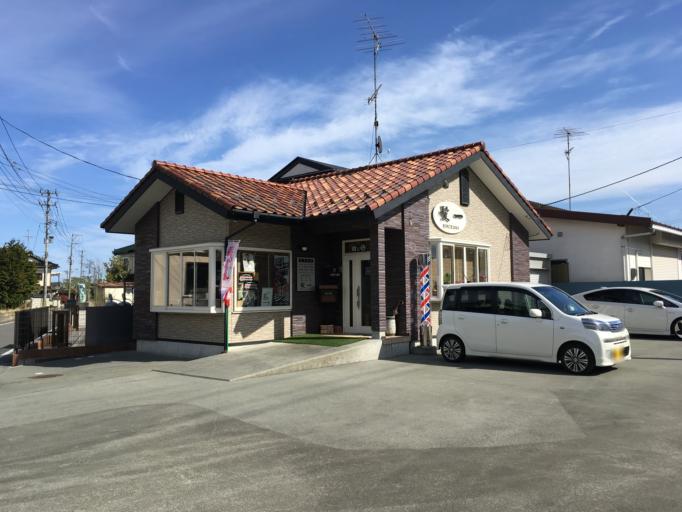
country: JP
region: Fukushima
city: Namie
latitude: 37.5622
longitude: 140.9891
